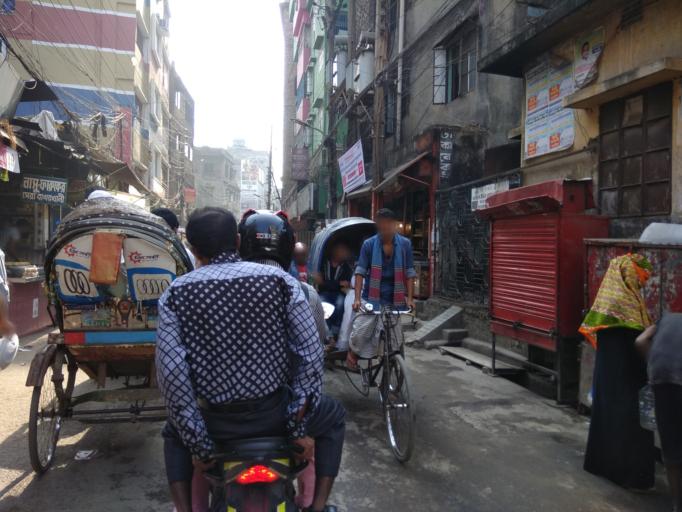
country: BD
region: Dhaka
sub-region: Dhaka
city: Dhaka
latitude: 23.7224
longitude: 90.3997
